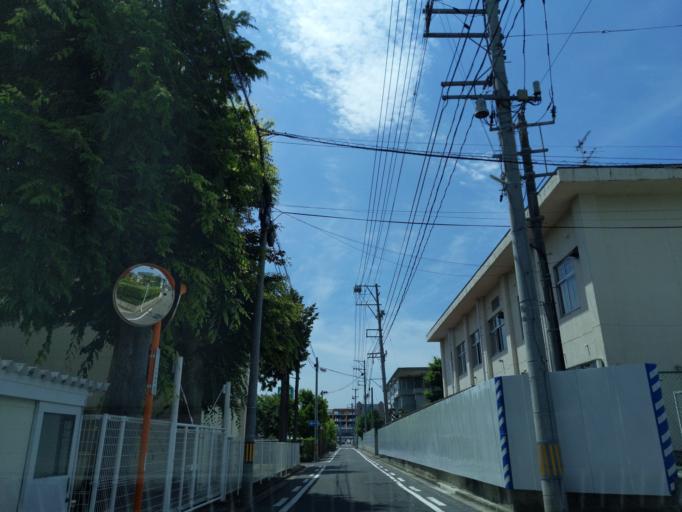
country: JP
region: Fukushima
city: Koriyama
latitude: 37.4008
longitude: 140.3707
